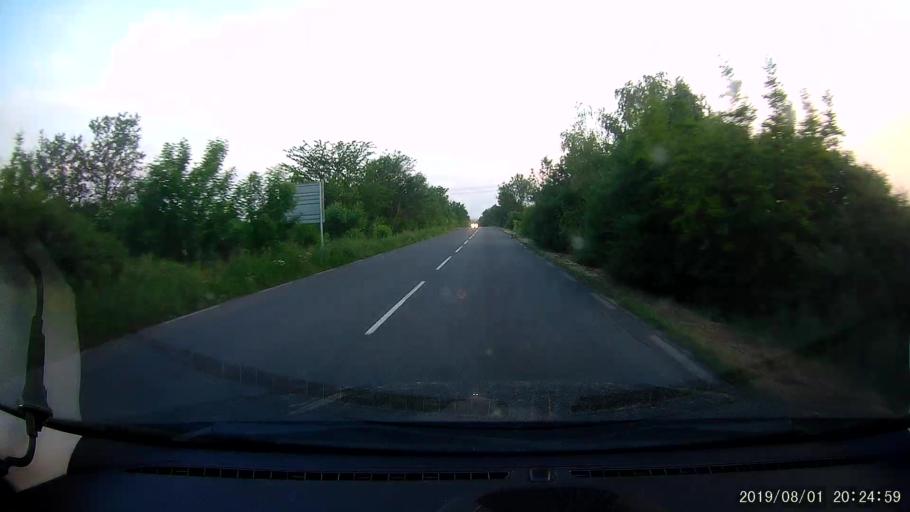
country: BG
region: Yambol
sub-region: Obshtina Elkhovo
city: Elkhovo
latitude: 42.2230
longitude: 26.5902
